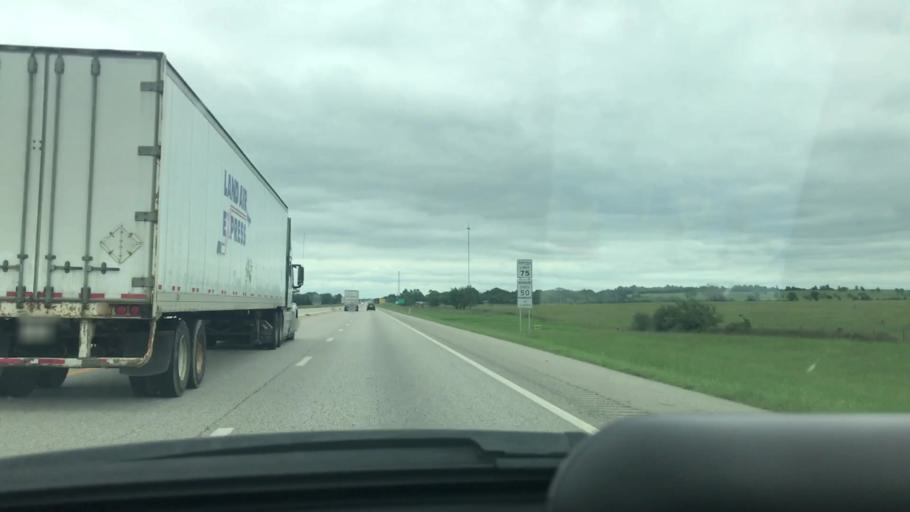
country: US
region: Oklahoma
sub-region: Craig County
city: Vinita
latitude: 36.5707
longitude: -95.2101
